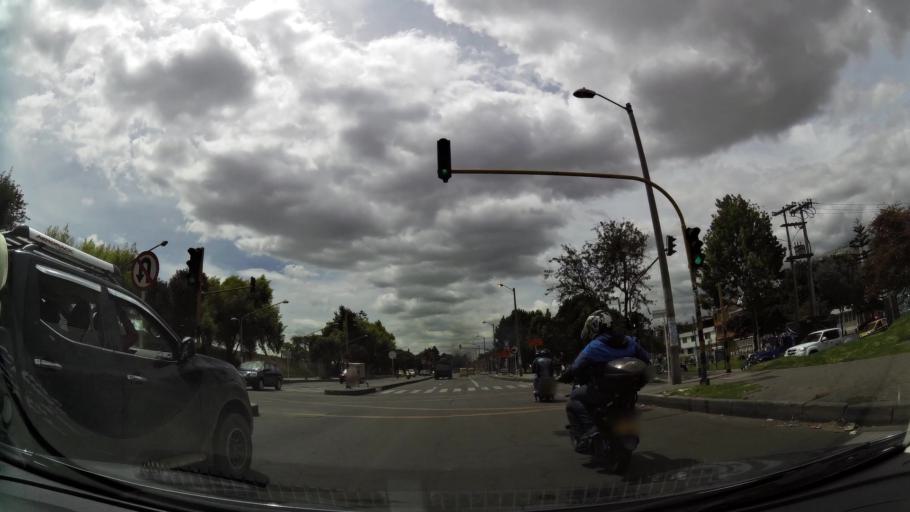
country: CO
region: Cundinamarca
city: Funza
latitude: 4.7023
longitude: -74.1343
